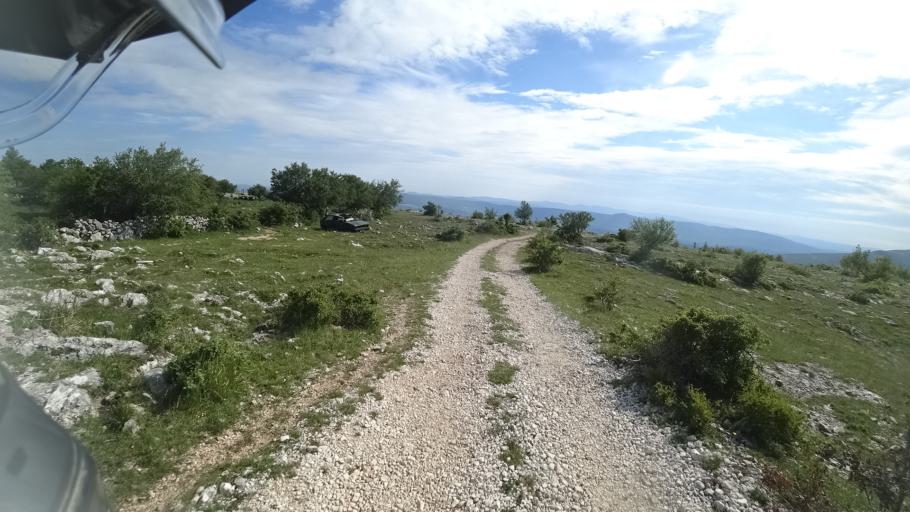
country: HR
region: Splitsko-Dalmatinska
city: Hrvace
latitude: 43.7805
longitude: 16.4459
